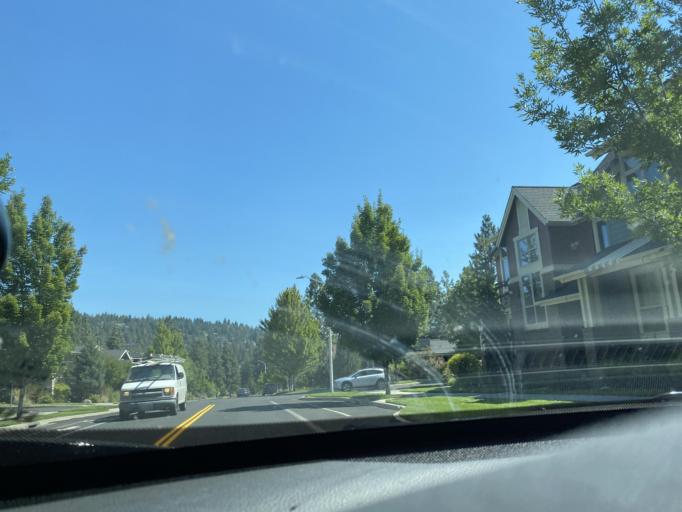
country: US
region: Oregon
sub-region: Deschutes County
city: Bend
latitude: 44.0607
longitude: -121.3483
